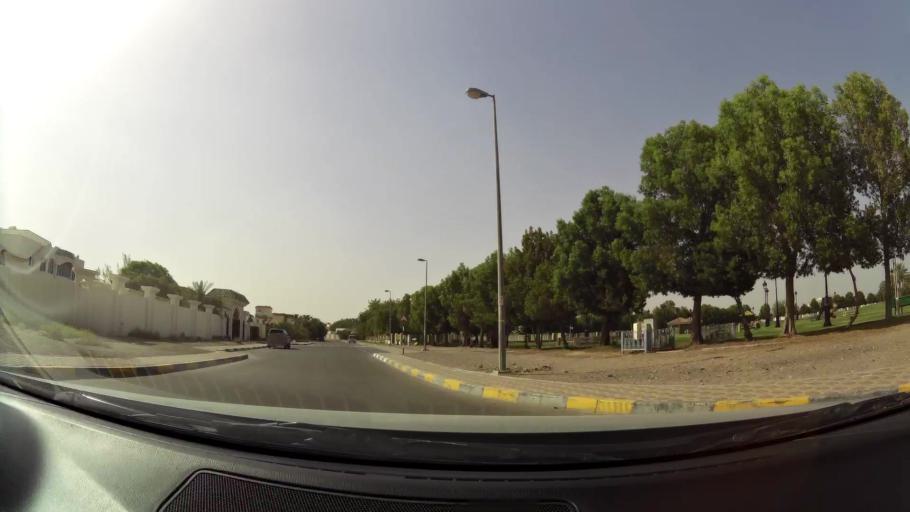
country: AE
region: Abu Dhabi
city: Al Ain
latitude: 24.2436
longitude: 55.6962
